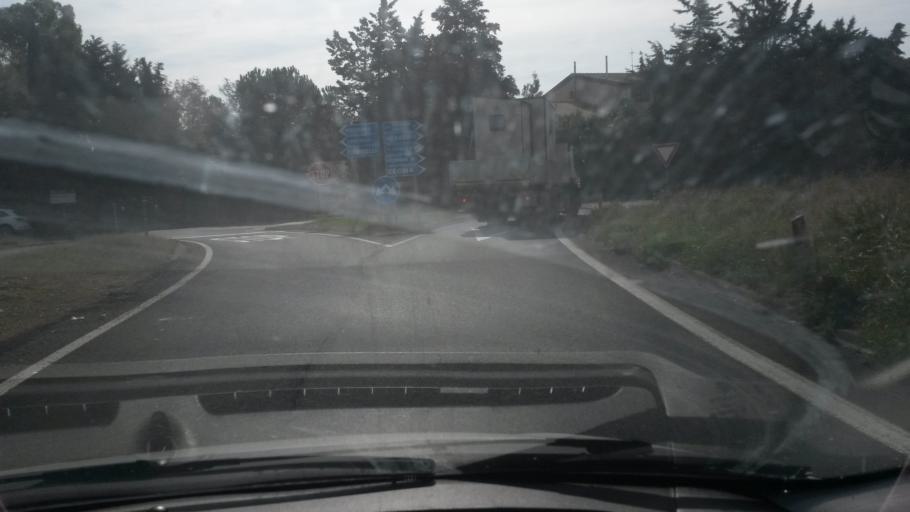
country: IT
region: Tuscany
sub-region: Provincia di Livorno
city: S.P. in Palazzi
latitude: 43.3326
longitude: 10.5270
